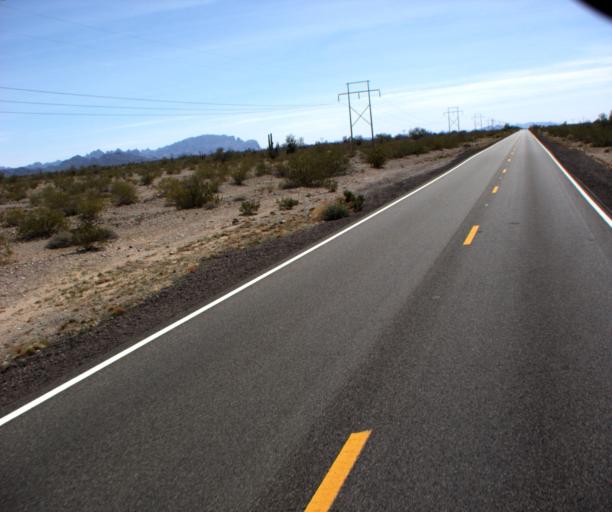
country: US
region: Arizona
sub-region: La Paz County
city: Quartzsite
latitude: 33.5643
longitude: -114.2170
